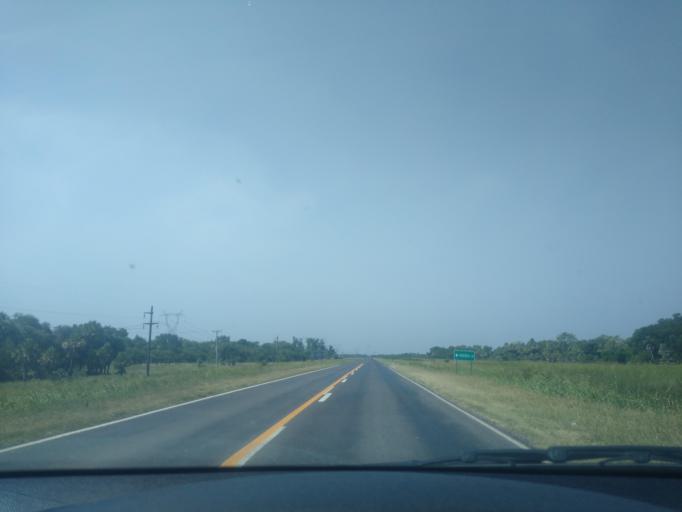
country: AR
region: Chaco
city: Fontana
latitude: -27.5727
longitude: -59.1556
